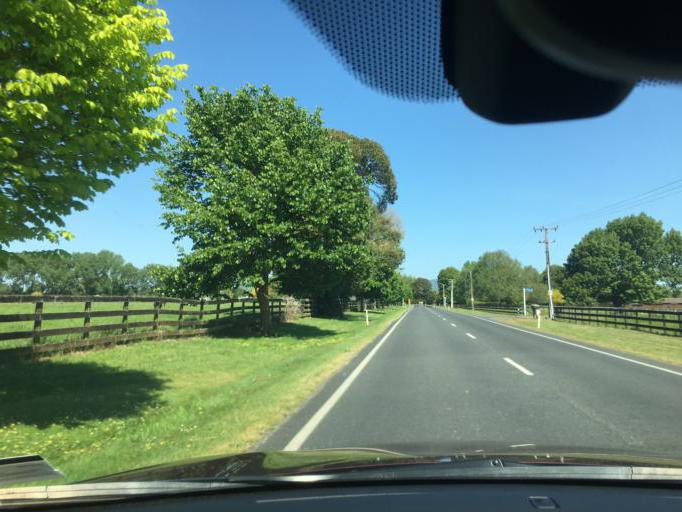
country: NZ
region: Waikato
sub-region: Waipa District
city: Cambridge
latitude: -37.9122
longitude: 175.4572
